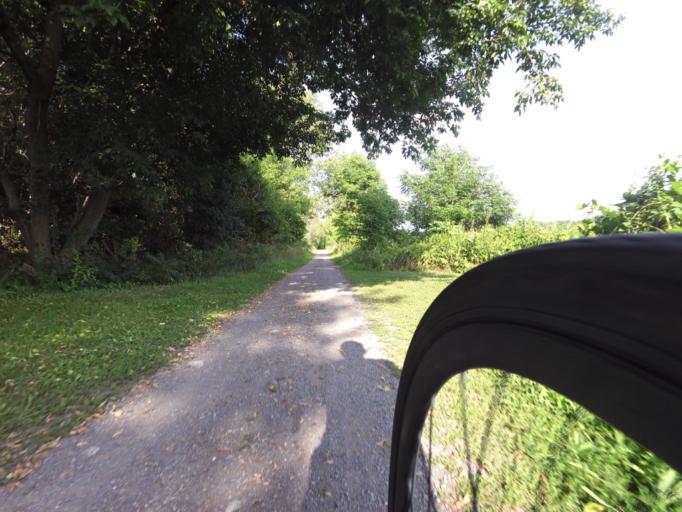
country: CA
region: Ontario
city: Kingston
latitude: 44.4158
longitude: -76.5869
